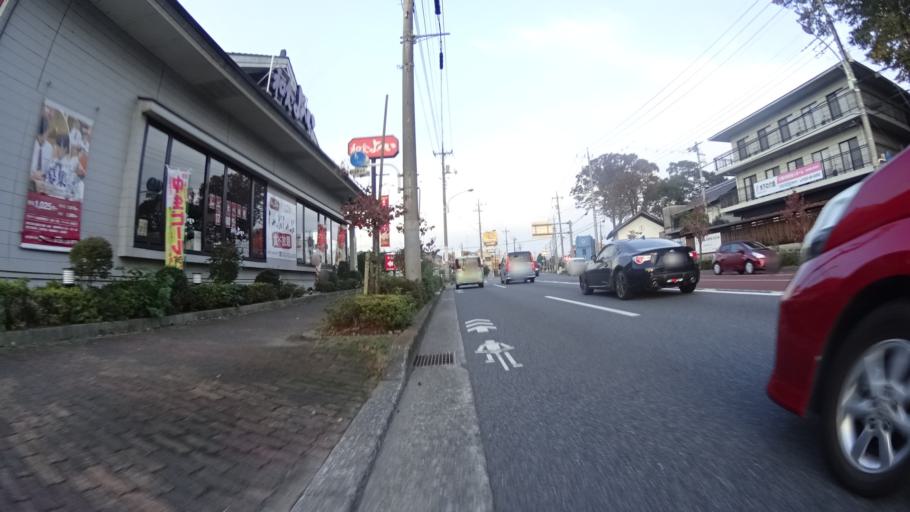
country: JP
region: Tokyo
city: Fussa
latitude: 35.7206
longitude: 139.3169
